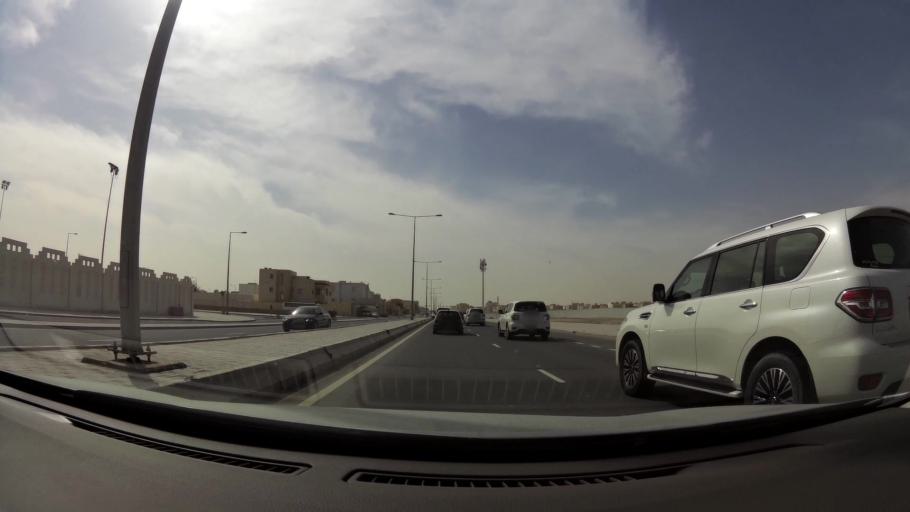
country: QA
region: Baladiyat ar Rayyan
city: Ar Rayyan
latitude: 25.3215
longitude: 51.3990
